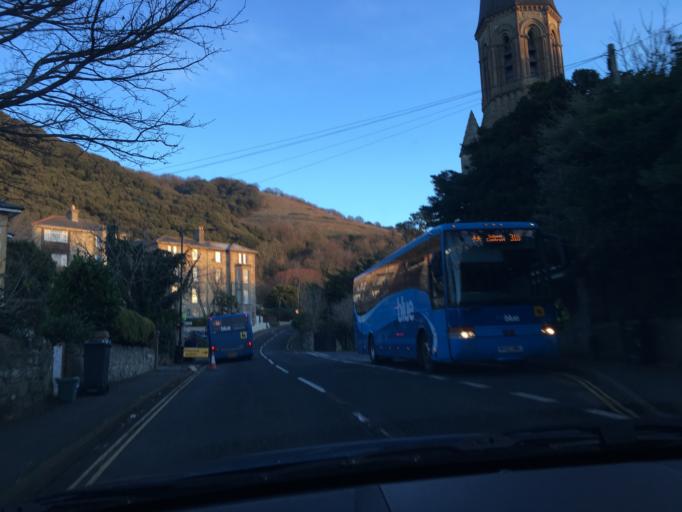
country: GB
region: England
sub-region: Isle of Wight
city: Ventnor
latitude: 50.5973
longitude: -1.1974
